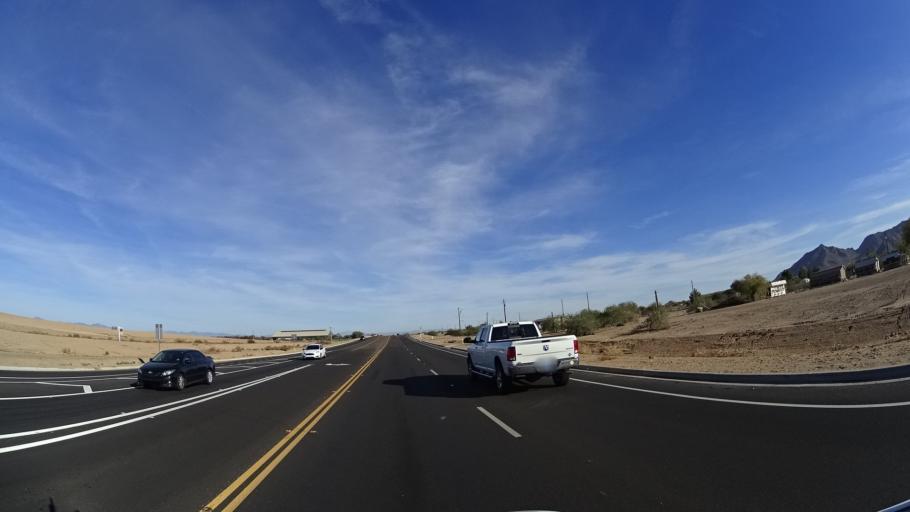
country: US
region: Arizona
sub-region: Maricopa County
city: Queen Creek
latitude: 33.2193
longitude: -111.6516
